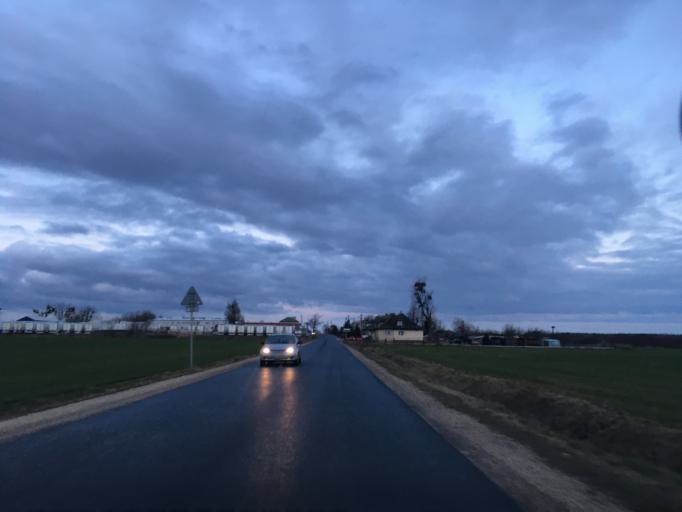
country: PL
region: Masovian Voivodeship
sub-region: Powiat pruszkowski
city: Owczarnia
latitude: 52.0798
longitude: 20.7263
